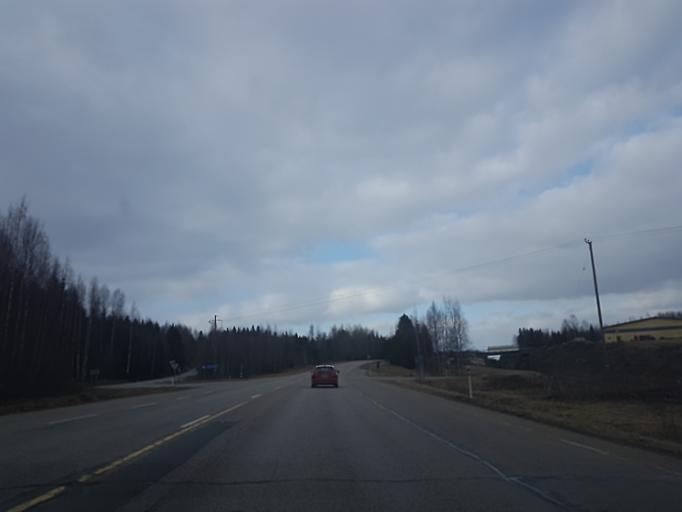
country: FI
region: South Karelia
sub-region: Imatra
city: Parikkala
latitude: 61.5017
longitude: 29.4900
